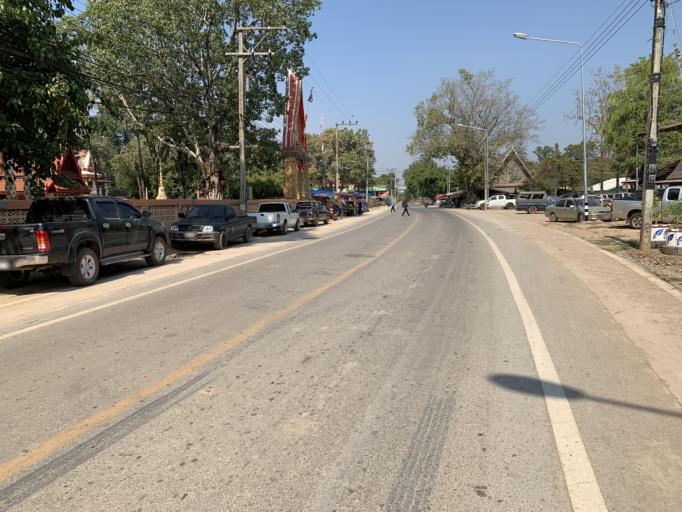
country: TH
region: Phitsanulok
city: Bang Krathum
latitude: 16.6427
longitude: 100.3203
